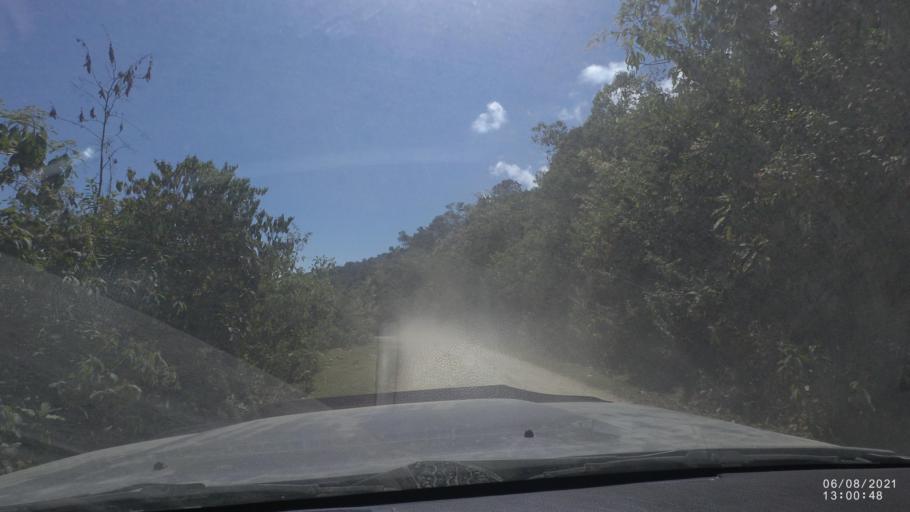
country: BO
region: Cochabamba
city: Colchani
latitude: -16.7467
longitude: -66.6903
